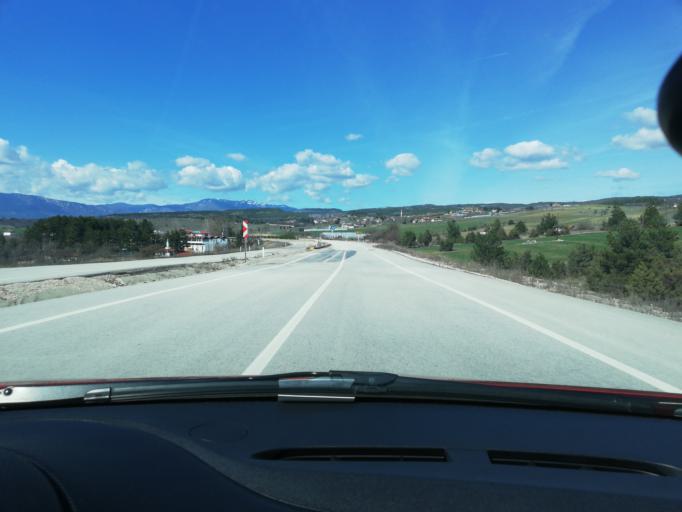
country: TR
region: Karabuk
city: Safranbolu
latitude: 41.2184
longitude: 32.7862
